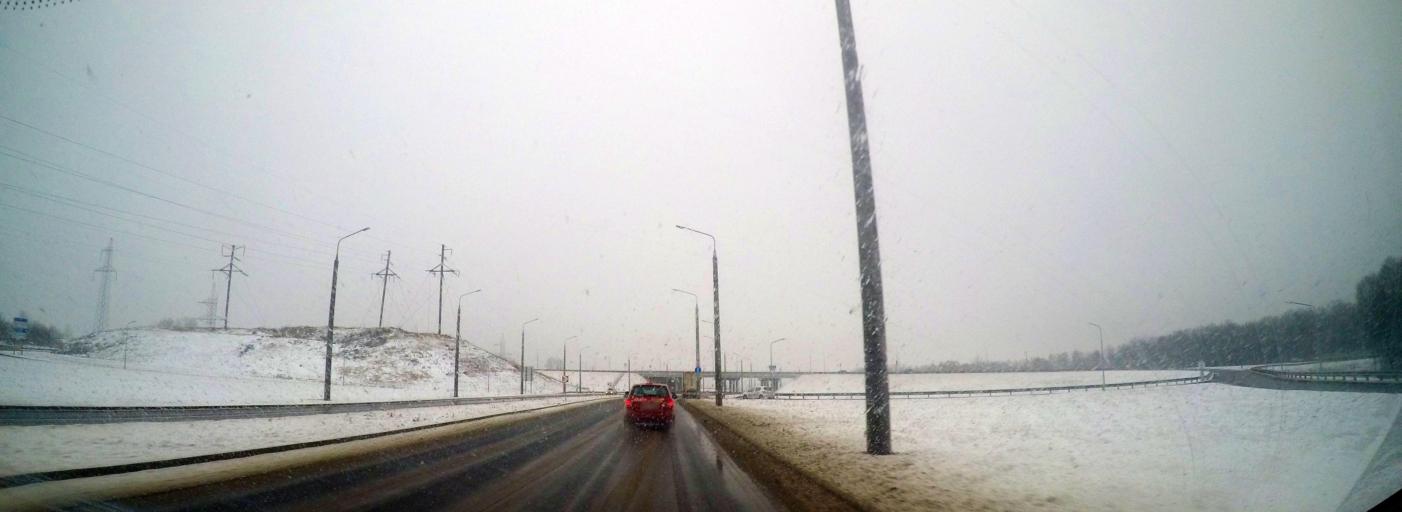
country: BY
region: Grodnenskaya
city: Hrodna
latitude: 53.6671
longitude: 23.8875
